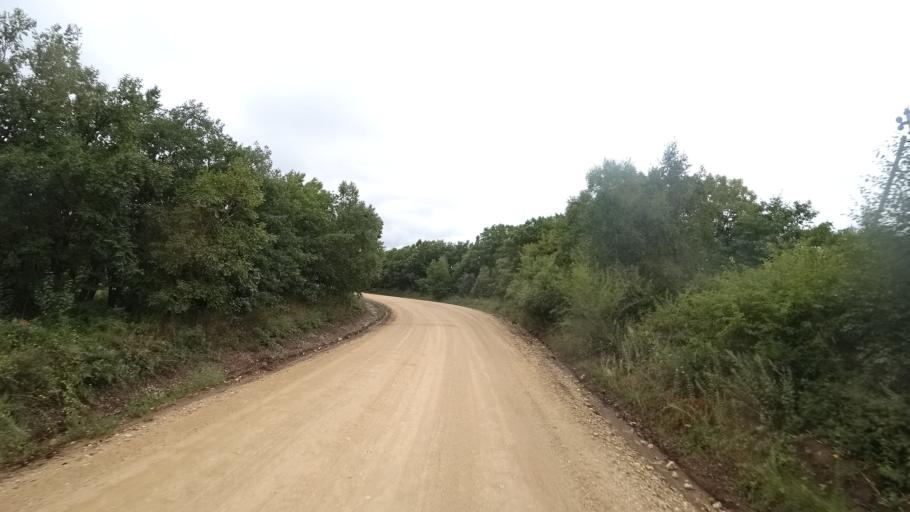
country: RU
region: Primorskiy
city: Chernigovka
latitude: 44.3412
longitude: 132.6207
